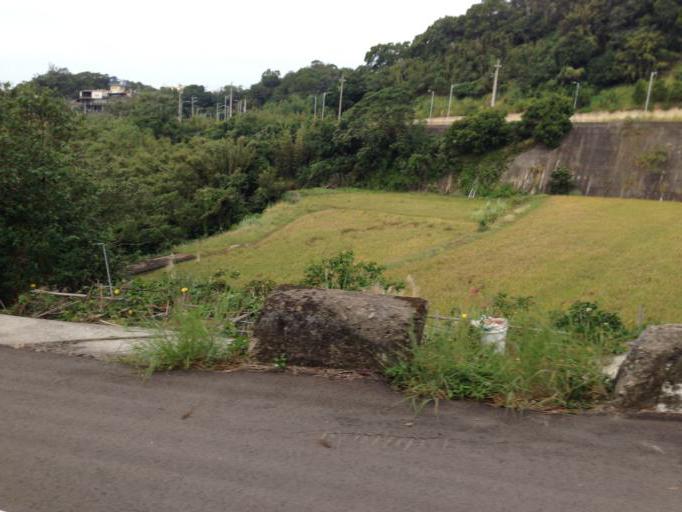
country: TW
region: Taiwan
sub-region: Hsinchu
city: Hsinchu
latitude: 24.7487
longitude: 120.9606
